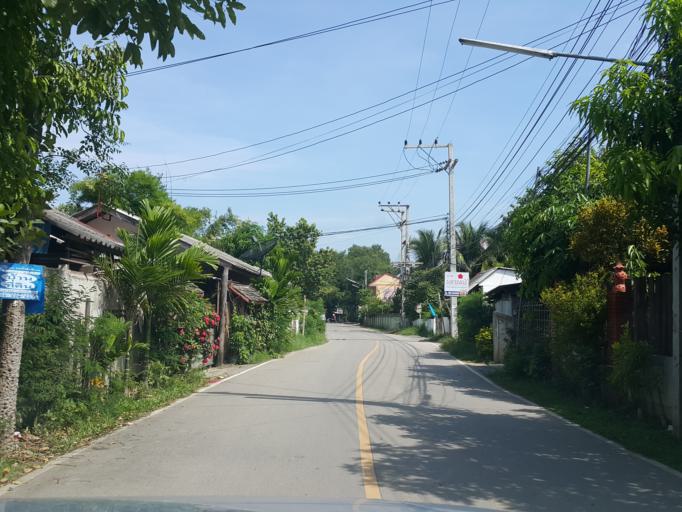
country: TH
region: Chiang Mai
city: Saraphi
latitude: 18.7487
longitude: 99.0508
